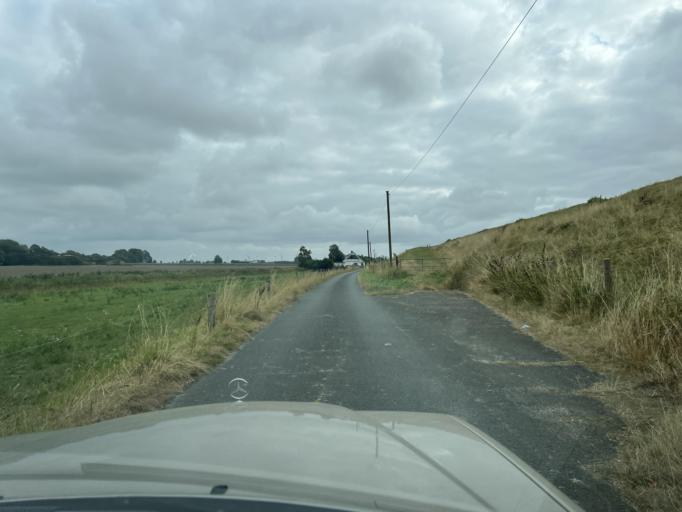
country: DE
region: Schleswig-Holstein
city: Groven
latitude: 54.3208
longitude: 8.9850
